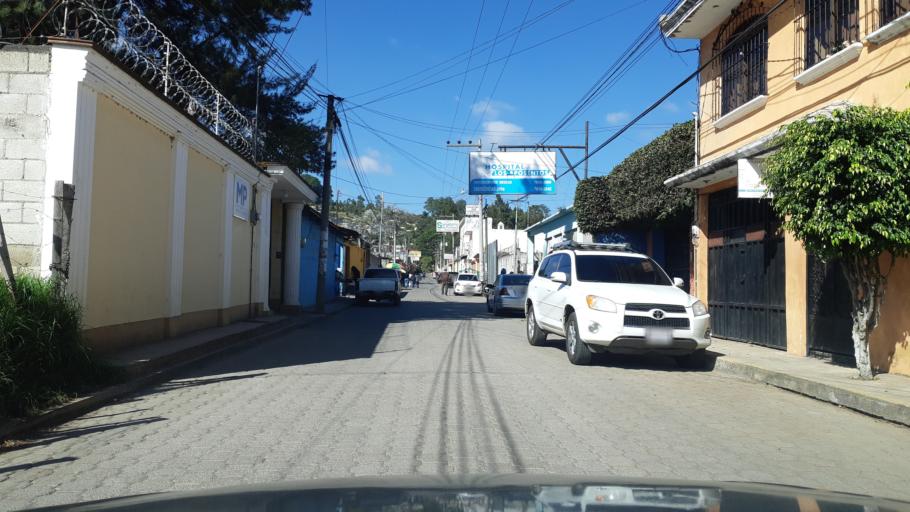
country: GT
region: Chimaltenango
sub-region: Municipio de Chimaltenango
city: Chimaltenango
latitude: 14.6525
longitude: -90.8155
